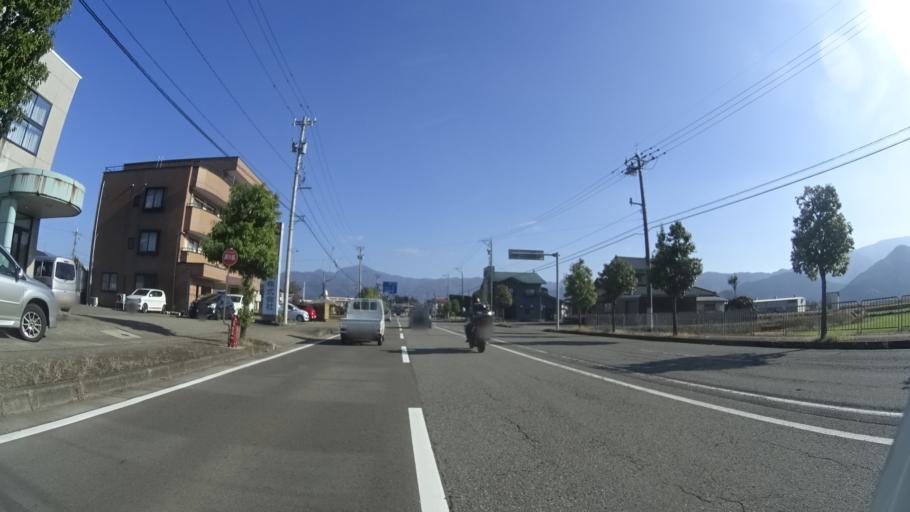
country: JP
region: Fukui
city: Ono
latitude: 35.9710
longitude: 136.4853
